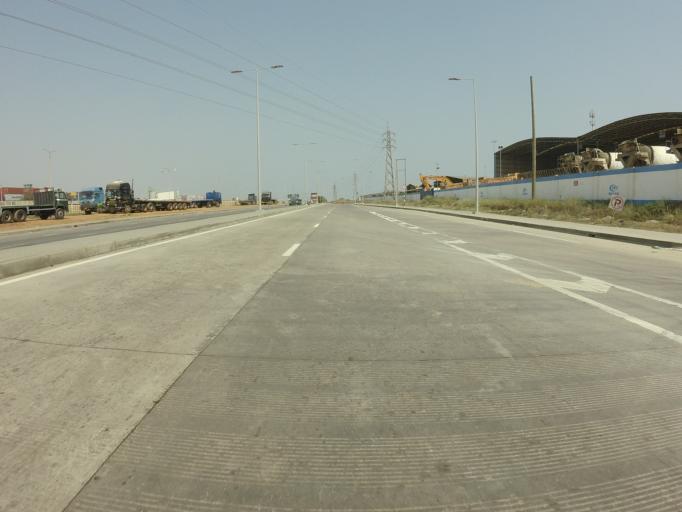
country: GH
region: Greater Accra
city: Tema
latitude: 5.6171
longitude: -0.0220
